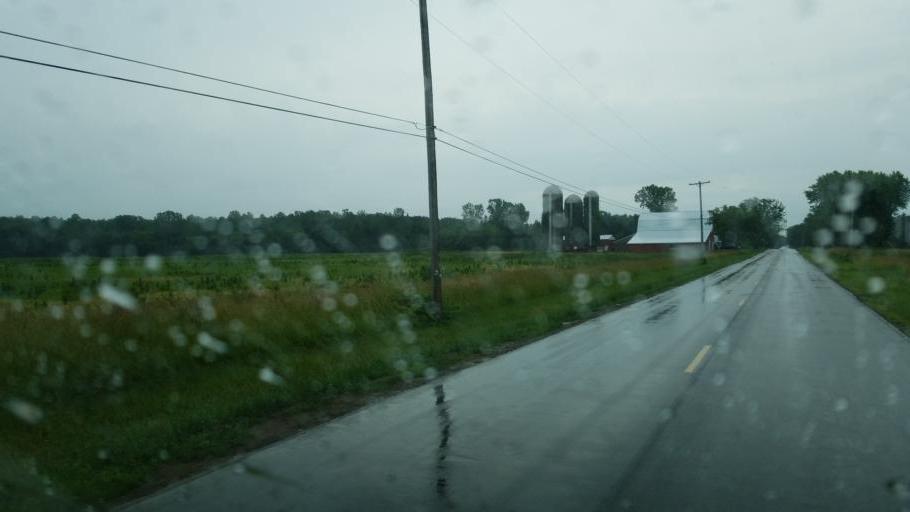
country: US
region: New York
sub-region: Niagara County
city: Ransomville
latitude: 43.2546
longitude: -78.8923
